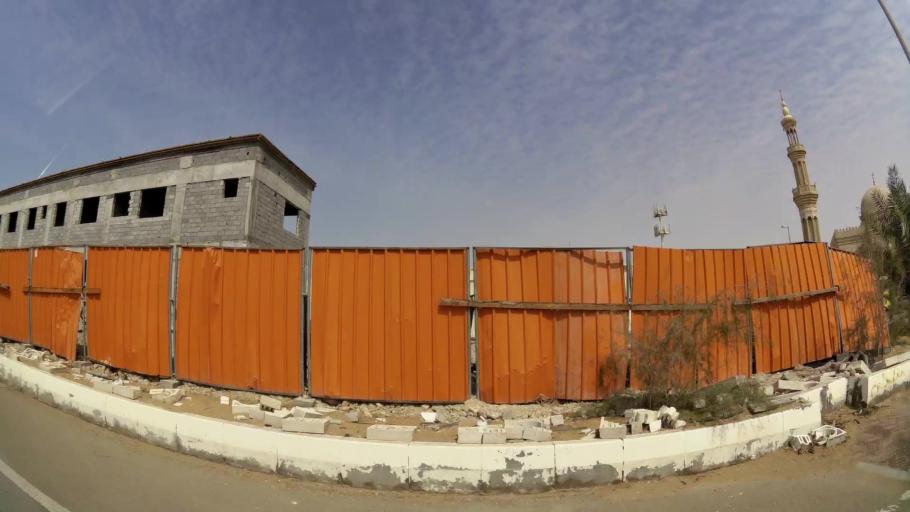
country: AE
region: Abu Dhabi
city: Abu Dhabi
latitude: 24.5251
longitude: 54.6646
